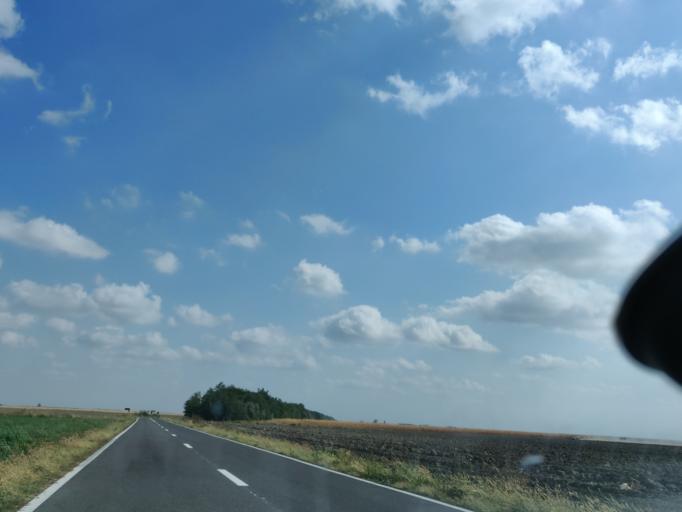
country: RO
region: Vrancea
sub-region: Comuna Ciorasti
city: Mihalceni
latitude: 45.4489
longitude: 27.3600
